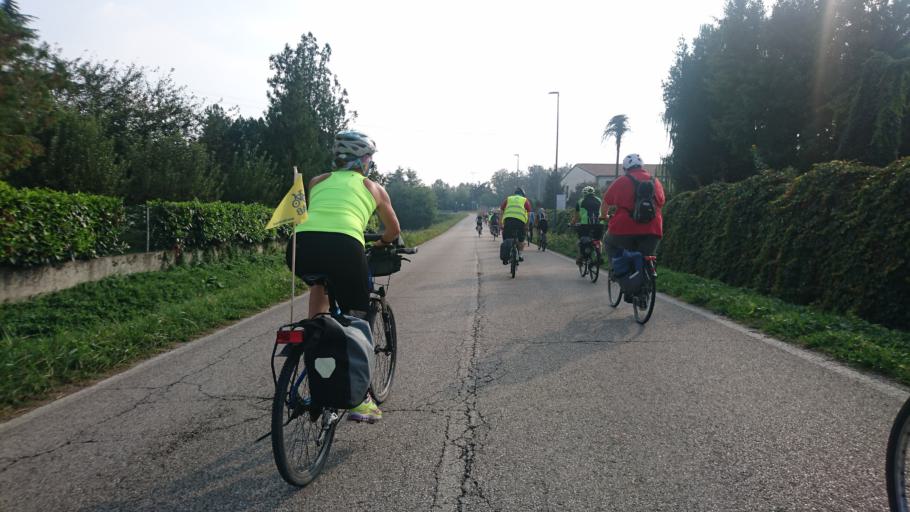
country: IT
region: Veneto
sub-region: Provincia di Rovigo
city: Arqua Polesine
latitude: 44.9999
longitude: 11.7364
